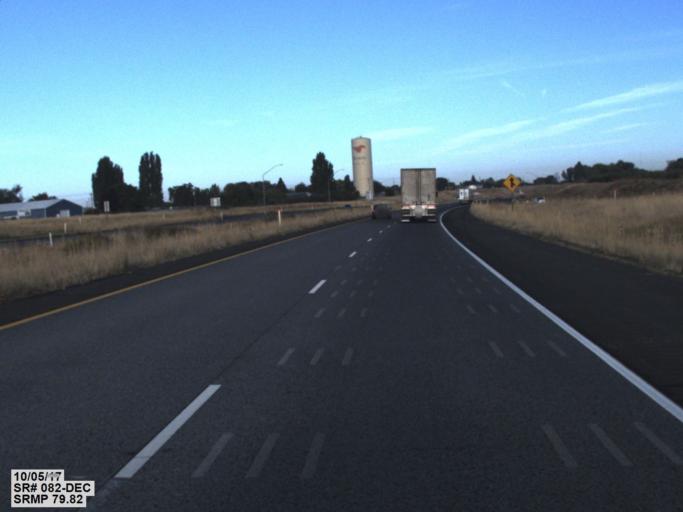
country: US
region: Washington
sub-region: Benton County
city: Prosser
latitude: 46.2231
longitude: -119.7928
